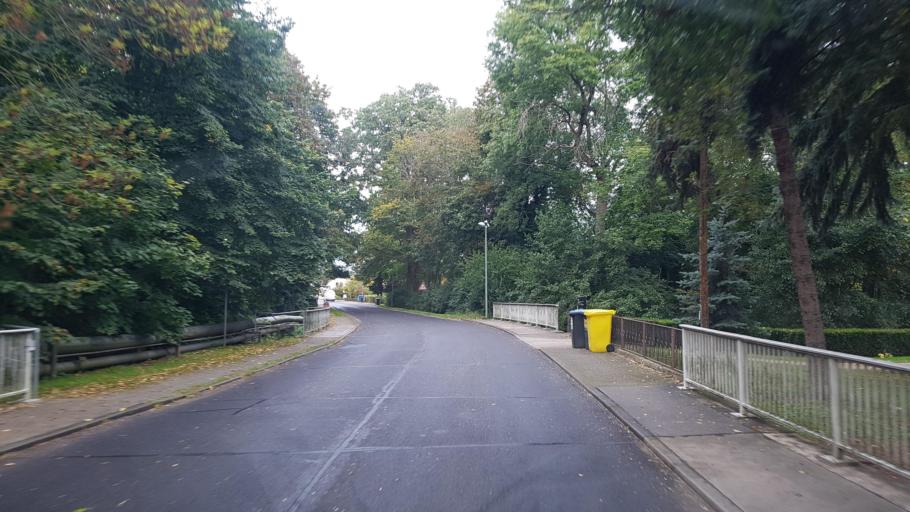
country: DE
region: Brandenburg
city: Kasel-Golzig
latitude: 51.9345
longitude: 13.7000
